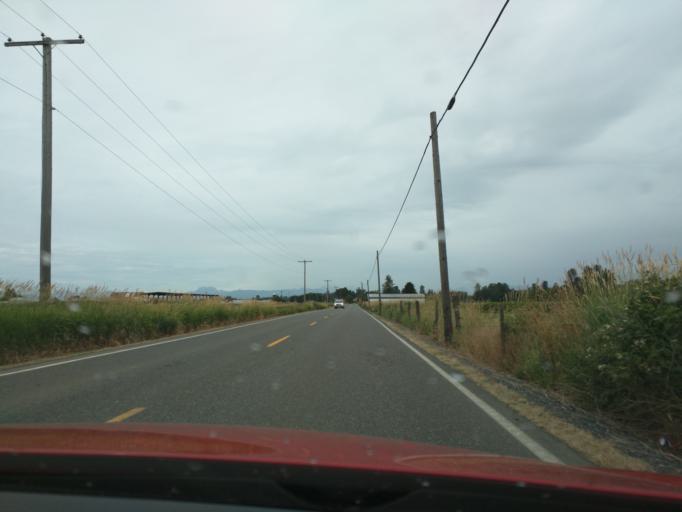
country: US
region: Washington
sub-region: Whatcom County
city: Nooksack
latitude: 48.9013
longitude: -122.3205
